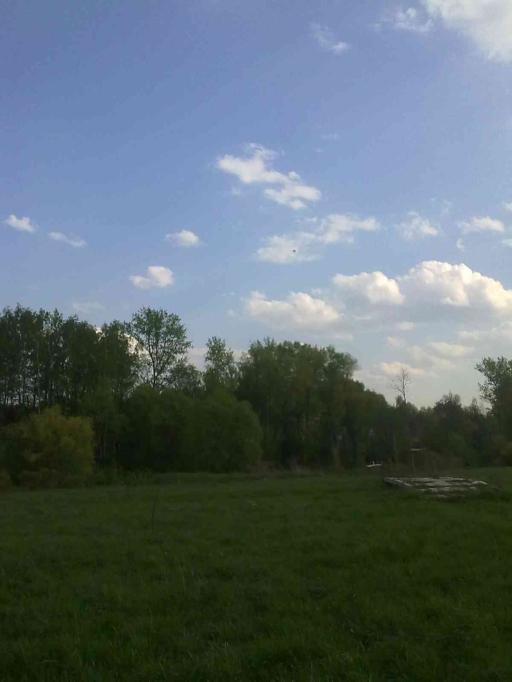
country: RU
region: Moscow
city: Vnukovo
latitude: 55.6008
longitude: 37.2161
